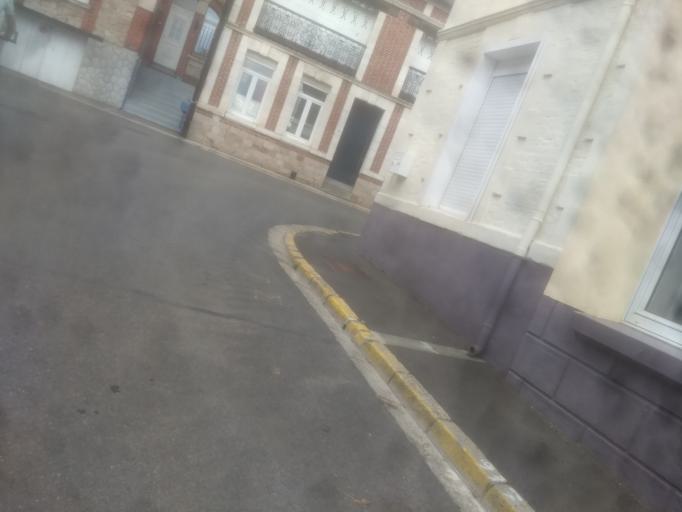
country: FR
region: Nord-Pas-de-Calais
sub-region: Departement du Pas-de-Calais
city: Maroeuil
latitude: 50.3246
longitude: 2.7037
